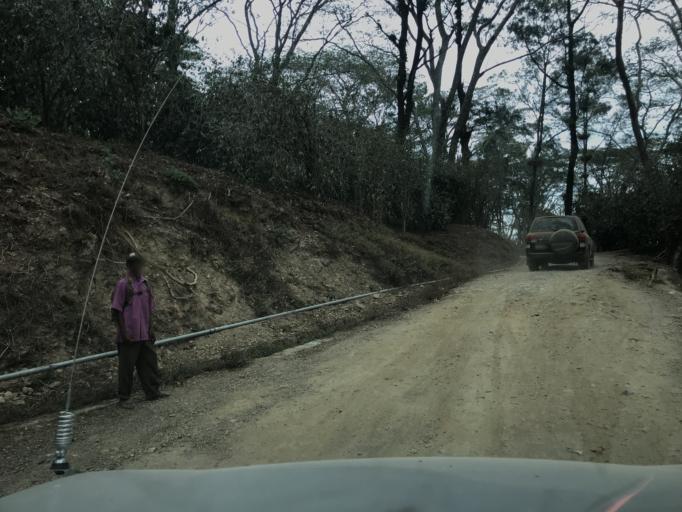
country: TL
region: Ermera
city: Gleno
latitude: -8.8362
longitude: 125.4466
